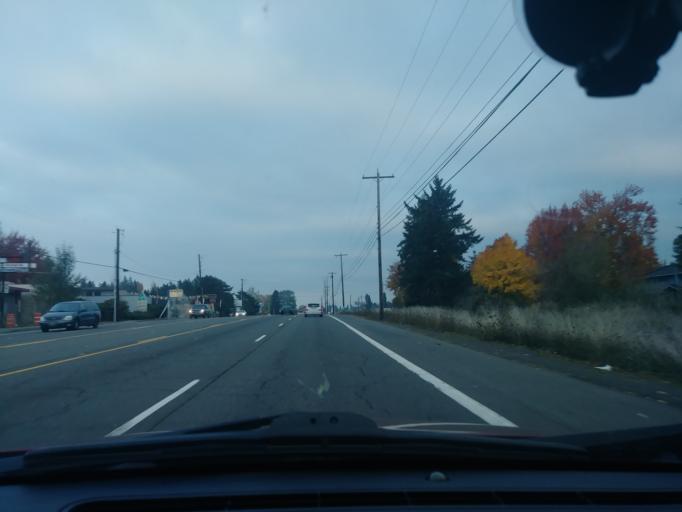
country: US
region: Oregon
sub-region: Washington County
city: Aloha
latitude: 45.4927
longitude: -122.8565
